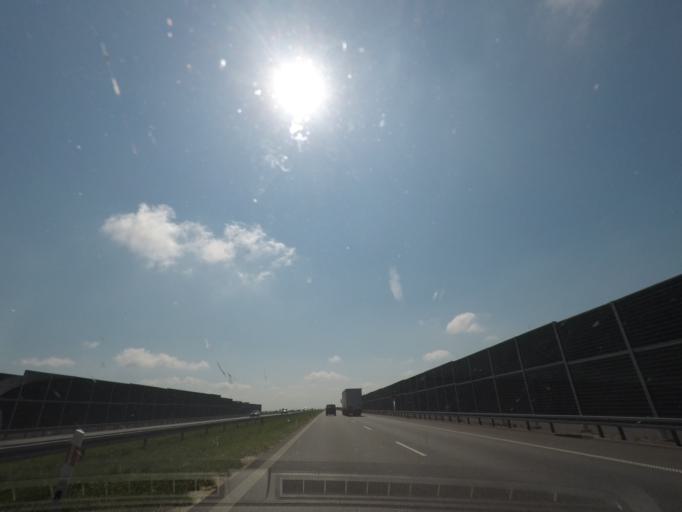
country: PL
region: Kujawsko-Pomorskie
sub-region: Powiat wloclawski
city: Czerniewice
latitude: 52.5445
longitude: 19.0502
